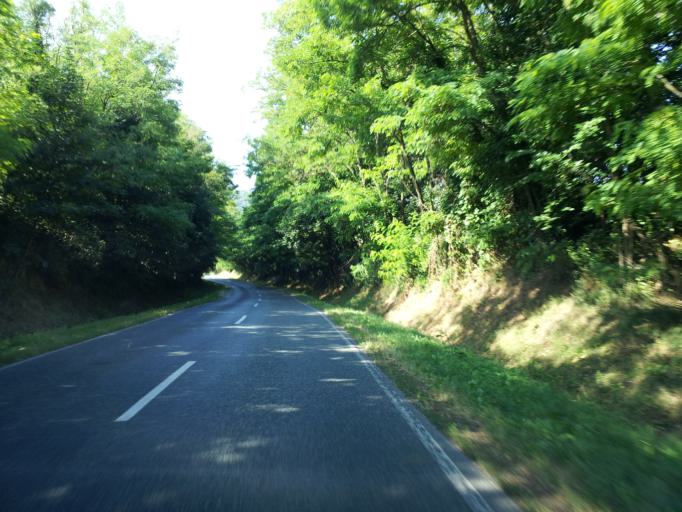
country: HU
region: Zala
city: Cserszegtomaj
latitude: 46.8763
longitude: 17.2209
